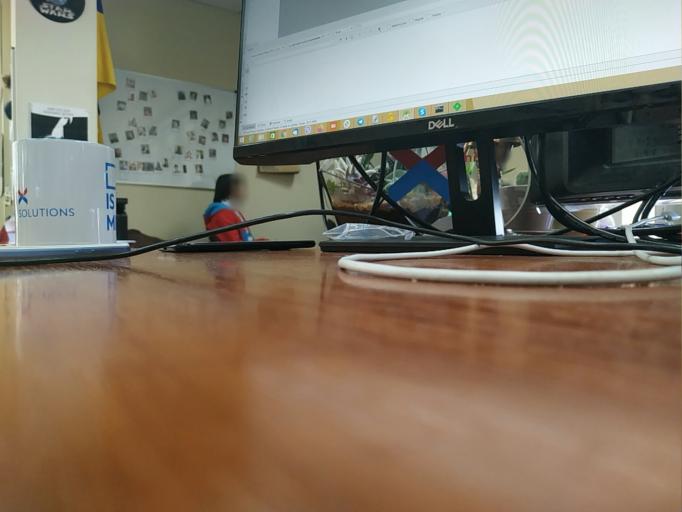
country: RU
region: Moskovskaya
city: Lozhki
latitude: 56.1916
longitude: 37.1901
